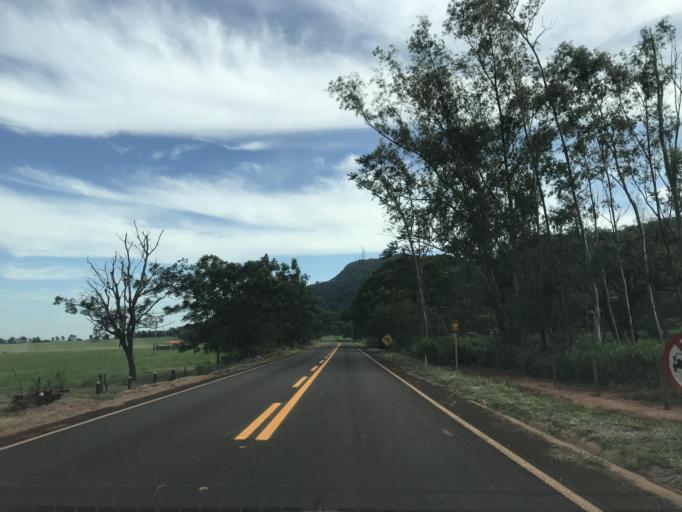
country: BR
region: Parana
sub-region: Terra Rica
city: Terra Rica
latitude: -22.7973
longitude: -52.6531
